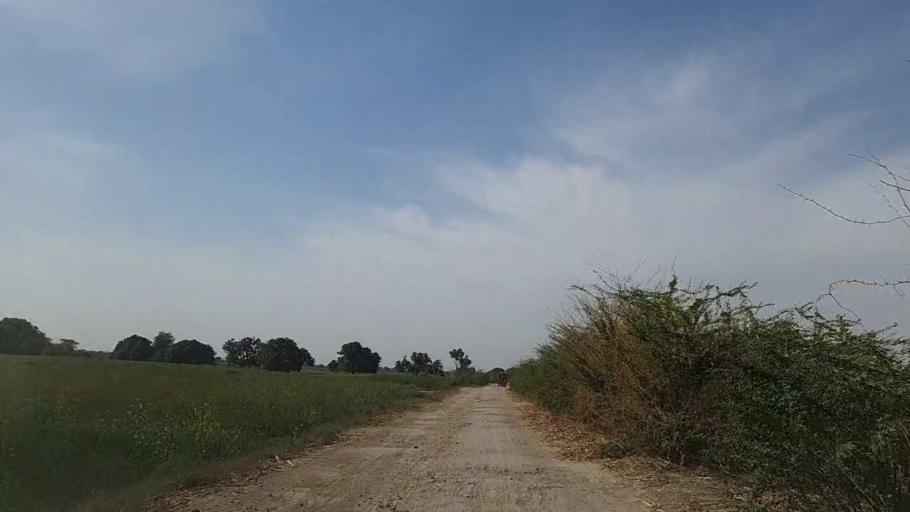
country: PK
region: Sindh
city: Samaro
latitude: 25.2332
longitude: 69.4261
